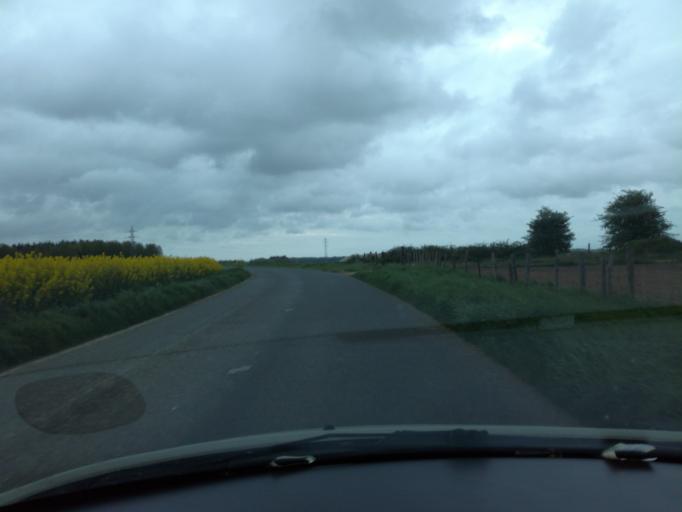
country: FR
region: Picardie
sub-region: Departement de la Somme
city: Poix-de-Picardie
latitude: 49.8178
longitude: 1.9687
